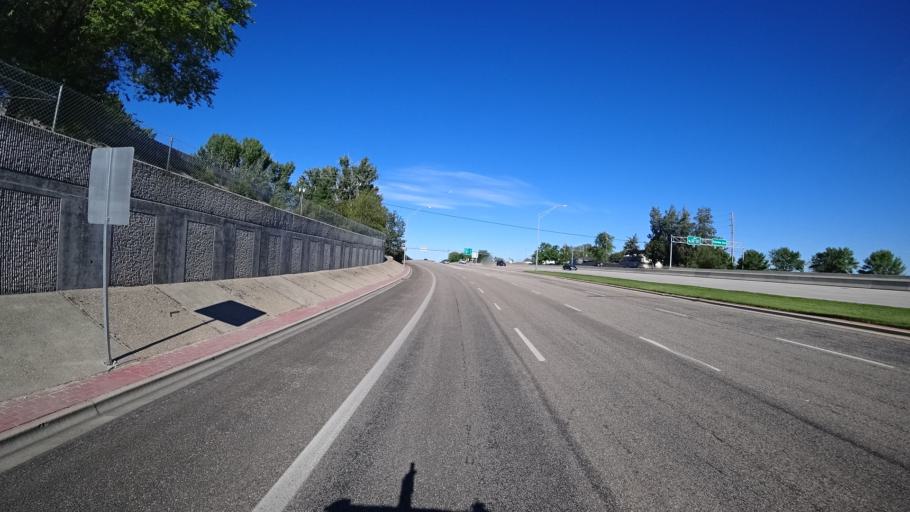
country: US
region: Idaho
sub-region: Ada County
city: Garden City
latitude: 43.6183
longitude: -116.2378
